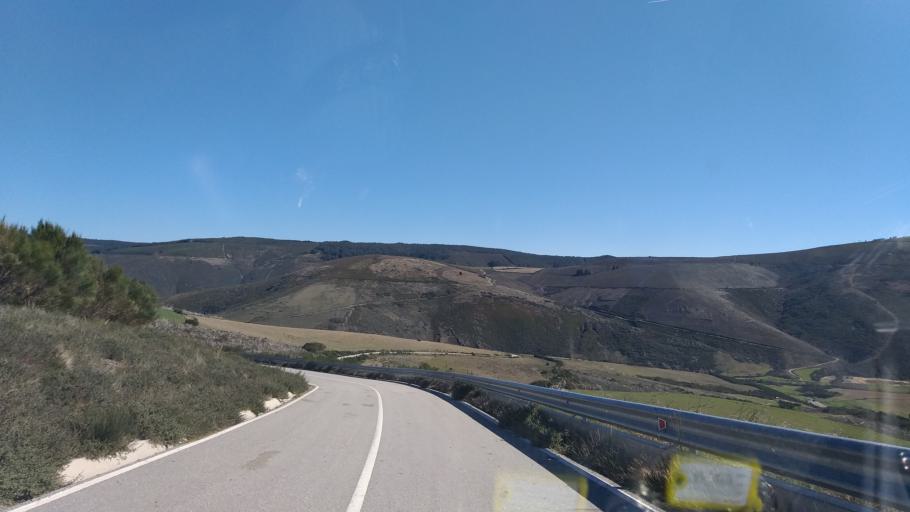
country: PT
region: Guarda
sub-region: Manteigas
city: Manteigas
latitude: 40.4631
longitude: -7.5025
